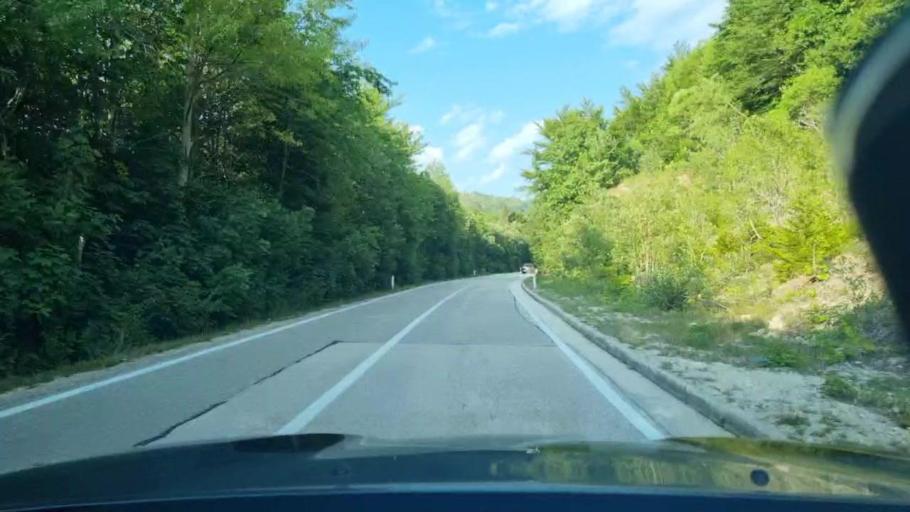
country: BA
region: Federation of Bosnia and Herzegovina
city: Glamoc
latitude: 44.1930
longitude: 16.8197
